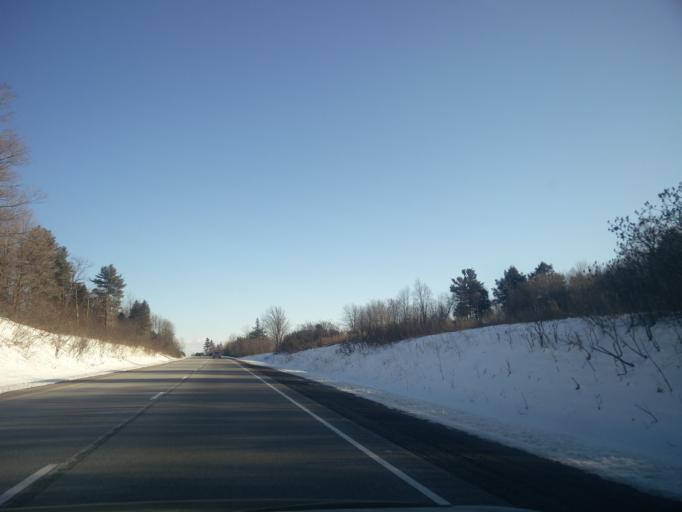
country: CA
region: Ontario
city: Prescott
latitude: 44.8971
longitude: -75.5731
